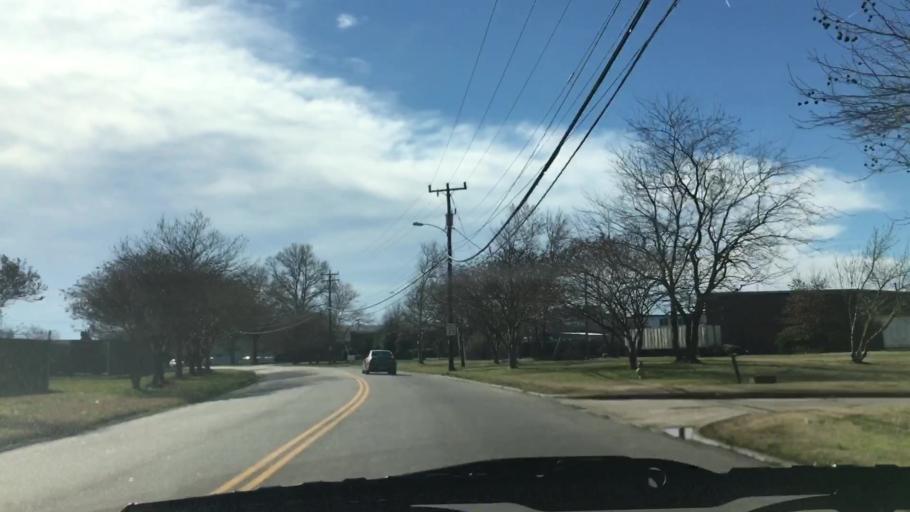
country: US
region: Virginia
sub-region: City of Norfolk
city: Norfolk
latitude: 36.8658
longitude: -76.2353
